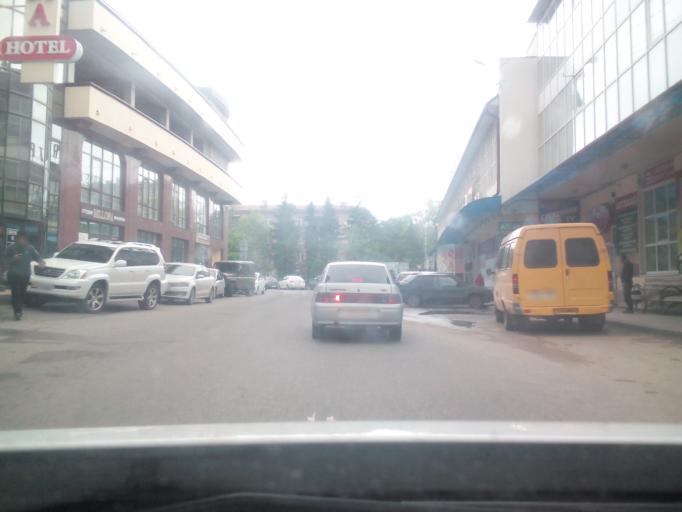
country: RU
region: Stavropol'skiy
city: Kislovodsk
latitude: 43.9082
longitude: 42.7080
